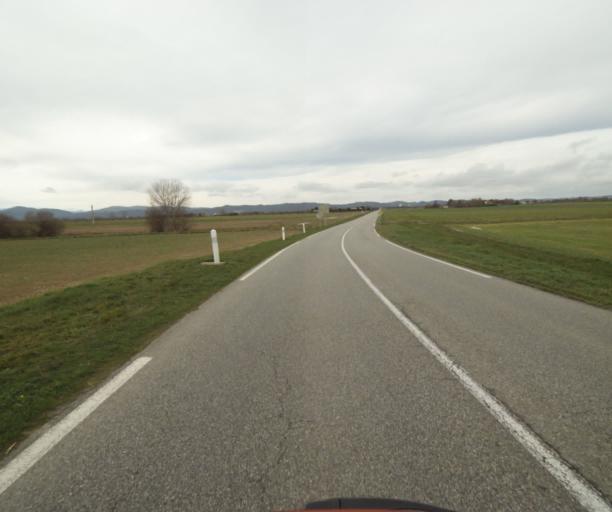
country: FR
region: Midi-Pyrenees
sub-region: Departement de l'Ariege
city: La Tour-du-Crieu
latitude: 43.0924
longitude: 1.6799
